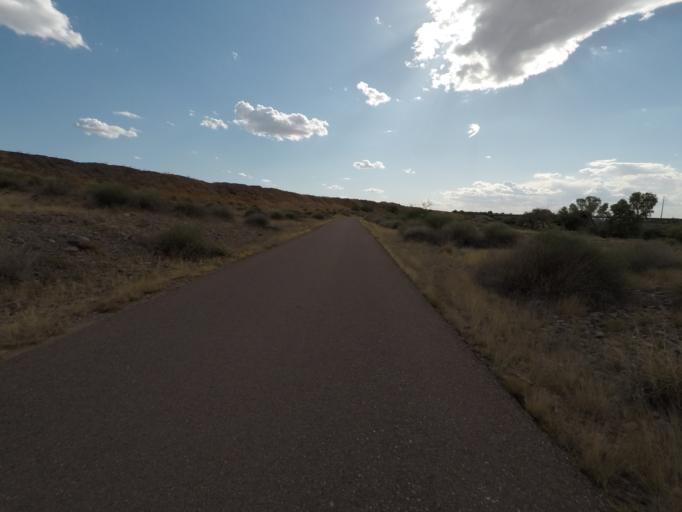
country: US
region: Arizona
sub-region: Maricopa County
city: Phoenix
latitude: 33.4162
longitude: -112.0397
